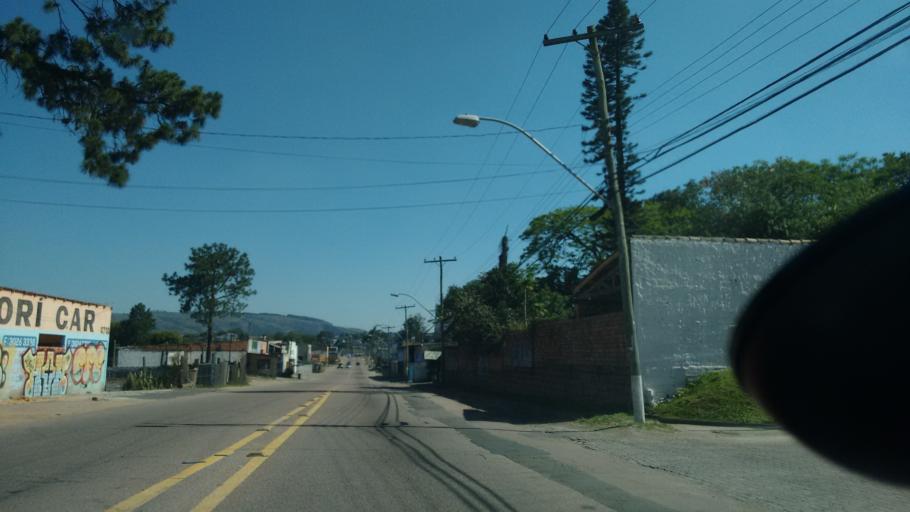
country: BR
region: Rio Grande do Sul
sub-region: Cachoeirinha
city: Cachoeirinha
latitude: -30.0066
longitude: -51.1278
